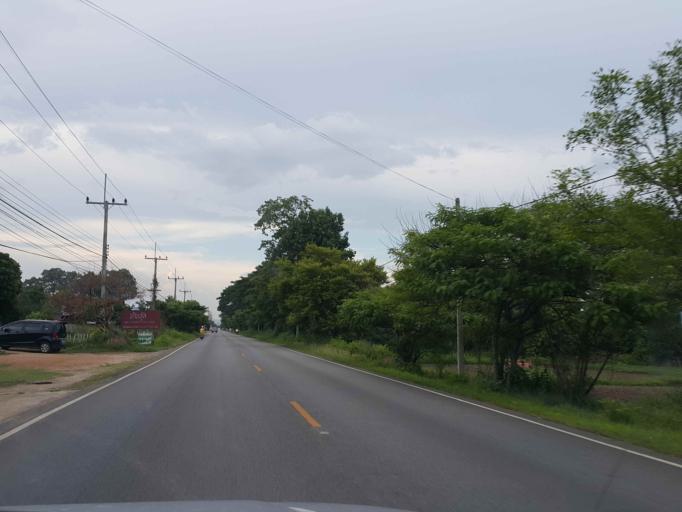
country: TH
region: Lampang
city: Ko Kha
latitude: 18.2536
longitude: 99.3880
